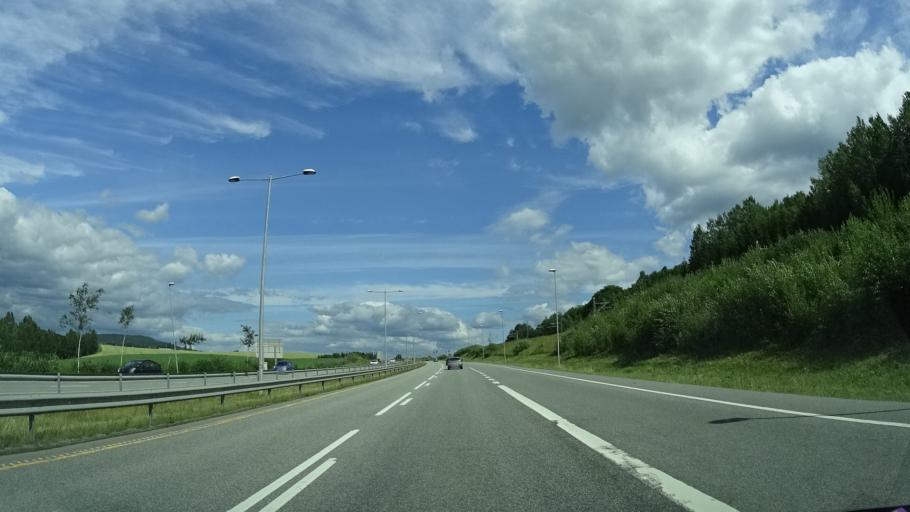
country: NO
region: Buskerud
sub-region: Drammen
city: Skoger
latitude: 59.6573
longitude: 10.2311
